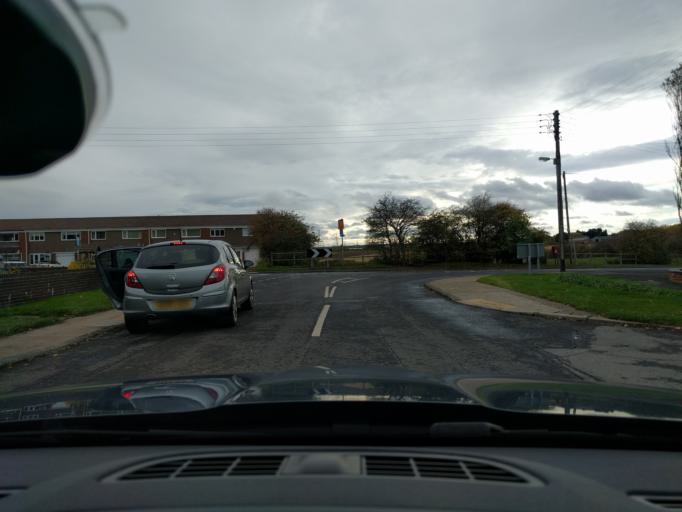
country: GB
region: England
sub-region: Northumberland
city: Ashington
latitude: 55.1450
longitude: -1.5498
